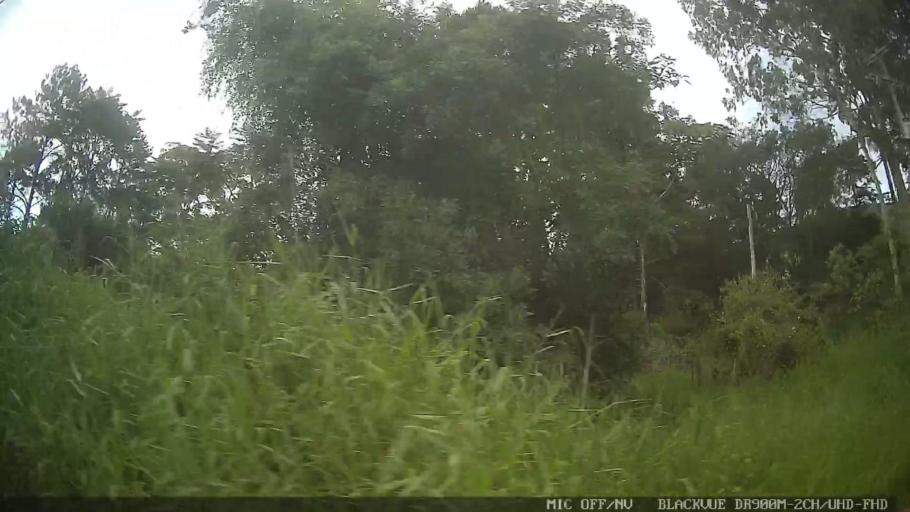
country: BR
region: Sao Paulo
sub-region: Bom Jesus Dos Perdoes
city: Bom Jesus dos Perdoes
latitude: -23.1475
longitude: -46.5069
